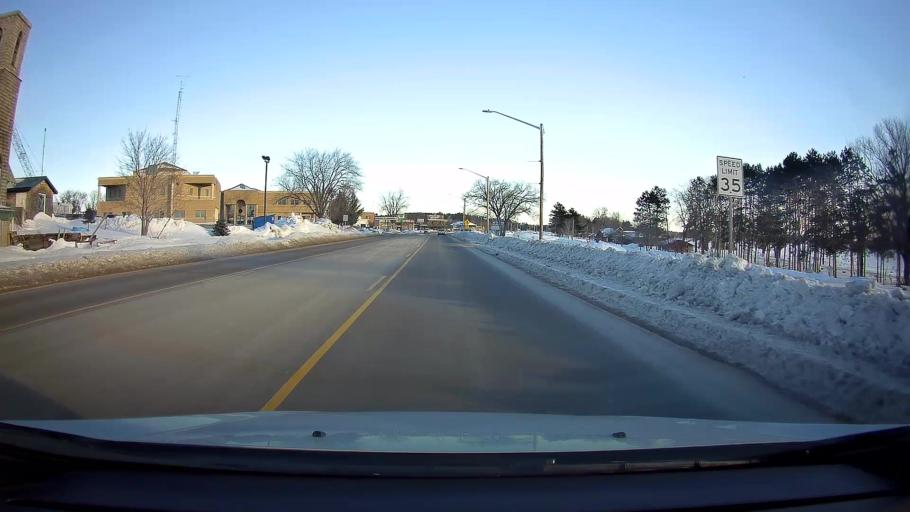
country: US
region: Wisconsin
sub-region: Washburn County
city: Shell Lake
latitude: 45.7405
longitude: -91.9250
